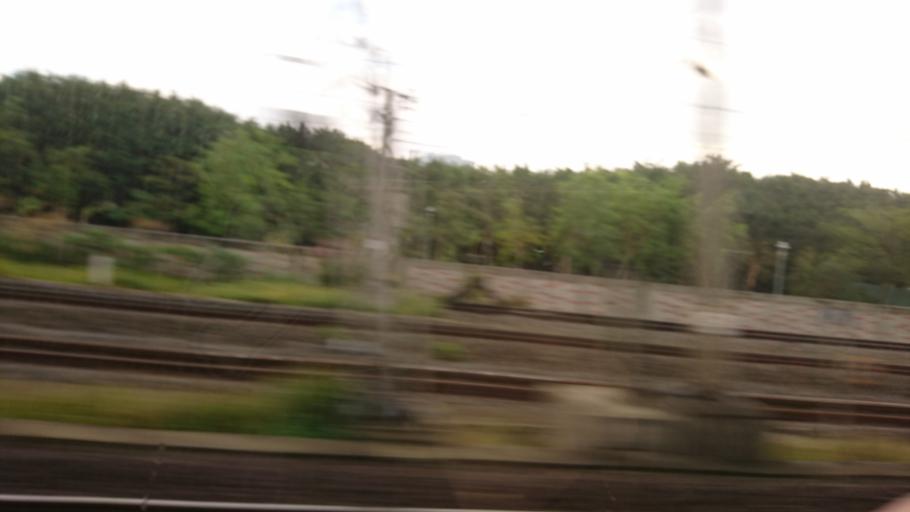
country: TW
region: Taiwan
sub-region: Hsinchu
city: Hsinchu
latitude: 24.8110
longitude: 120.9885
